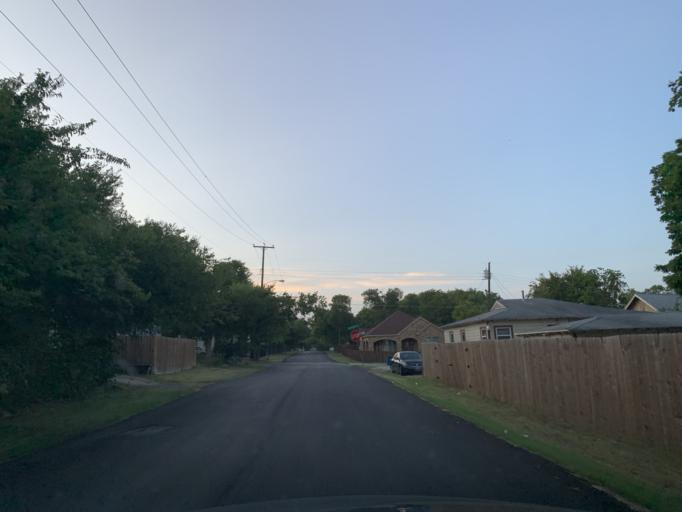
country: US
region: Texas
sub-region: Dallas County
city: Dallas
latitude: 32.6964
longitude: -96.8010
